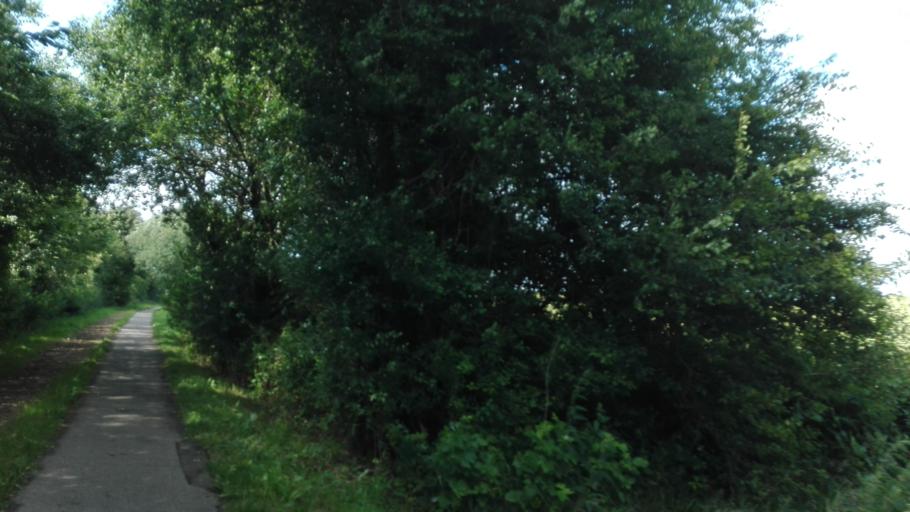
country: DK
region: Central Jutland
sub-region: Silkeborg Kommune
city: Virklund
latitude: 56.0861
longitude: 9.5307
